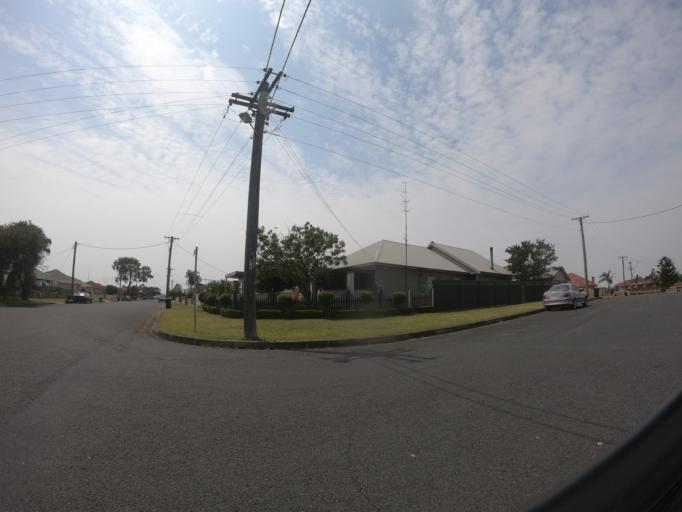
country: AU
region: New South Wales
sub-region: Wollongong
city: Fairy Meadow
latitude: -34.3873
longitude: 150.8862
